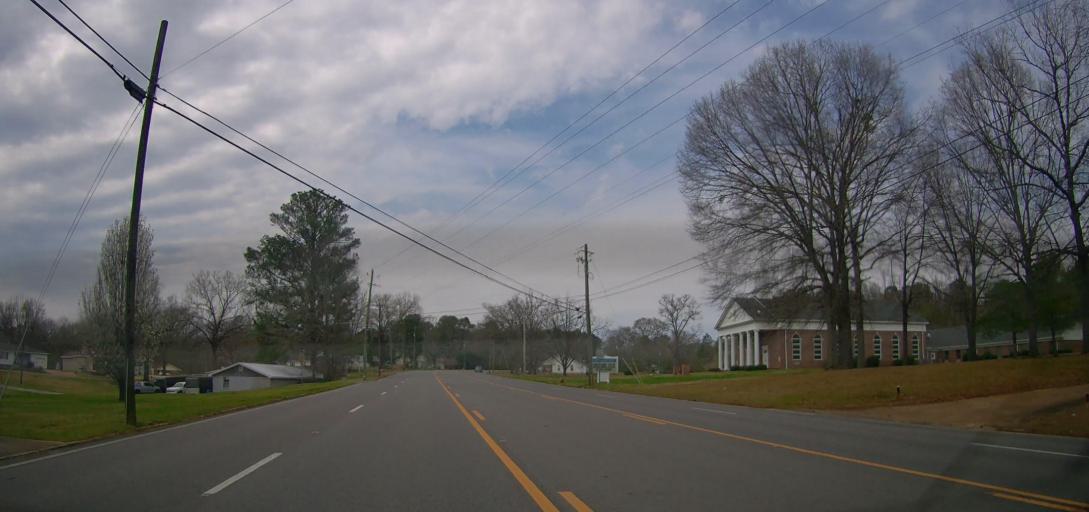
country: US
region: Alabama
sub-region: Marion County
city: Guin
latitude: 33.9766
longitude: -87.9162
